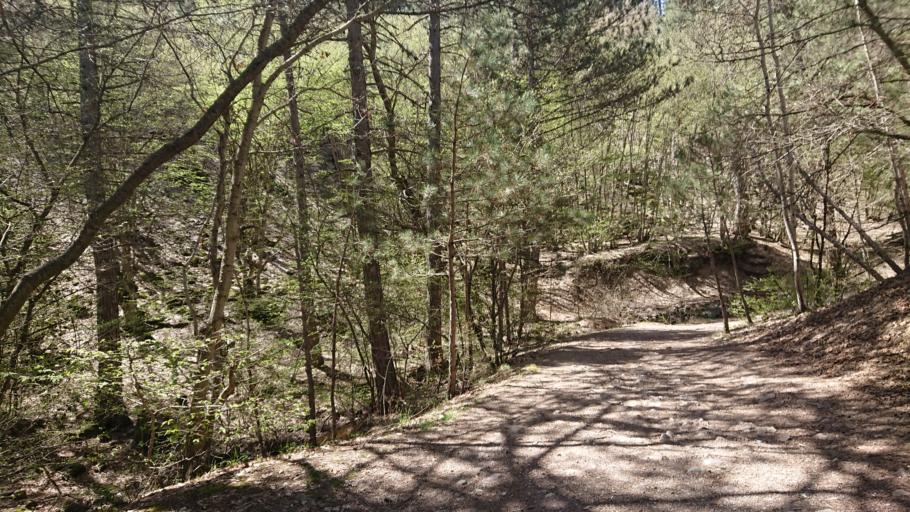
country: TR
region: Kuetahya
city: Sabuncu
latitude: 39.5089
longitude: 30.4197
